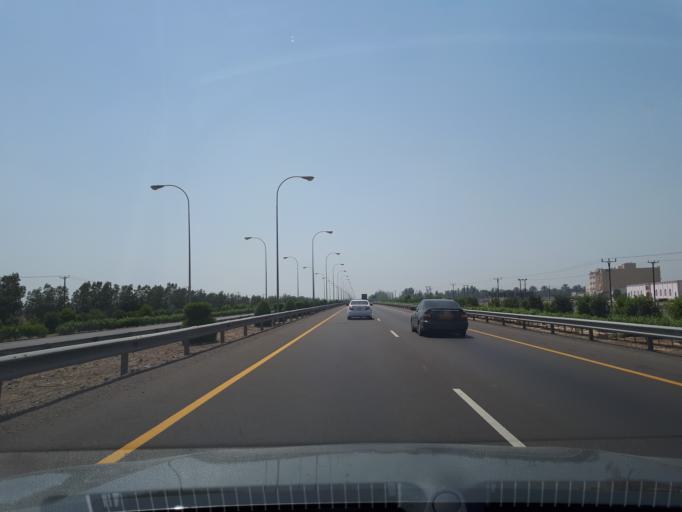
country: OM
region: Al Batinah
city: Al Sohar
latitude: 24.4037
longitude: 56.6580
